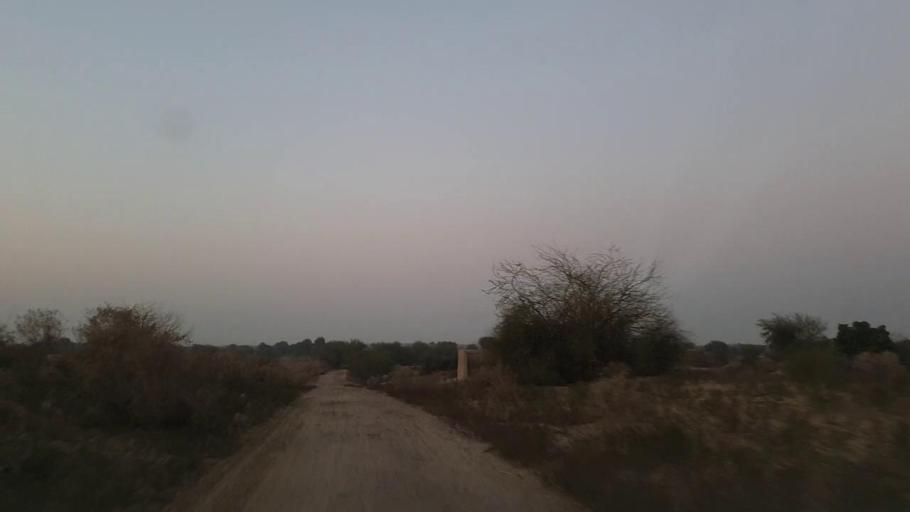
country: PK
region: Sindh
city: Bandhi
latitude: 26.6252
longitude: 68.3954
